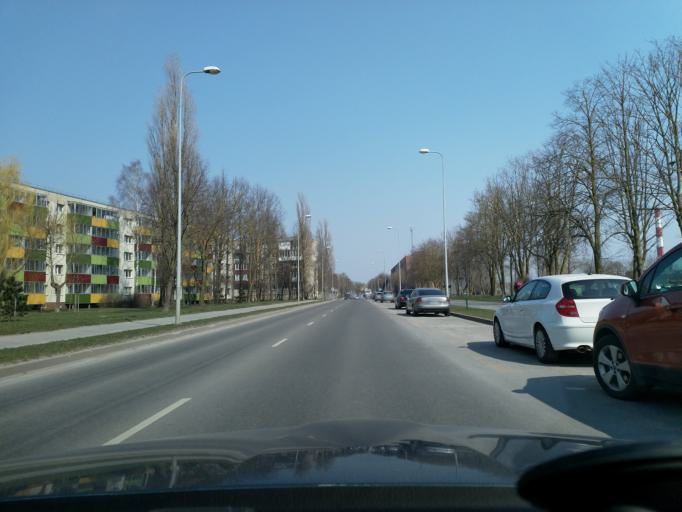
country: LT
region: Klaipedos apskritis
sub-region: Klaipeda
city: Klaipeda
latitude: 55.6960
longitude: 21.1575
